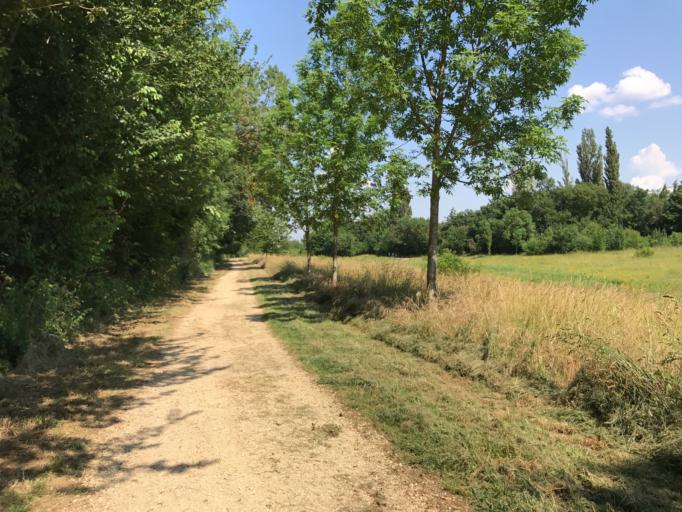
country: ES
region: Basque Country
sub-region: Provincia de Alava
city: Gasteiz / Vitoria
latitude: 42.8783
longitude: -2.6536
